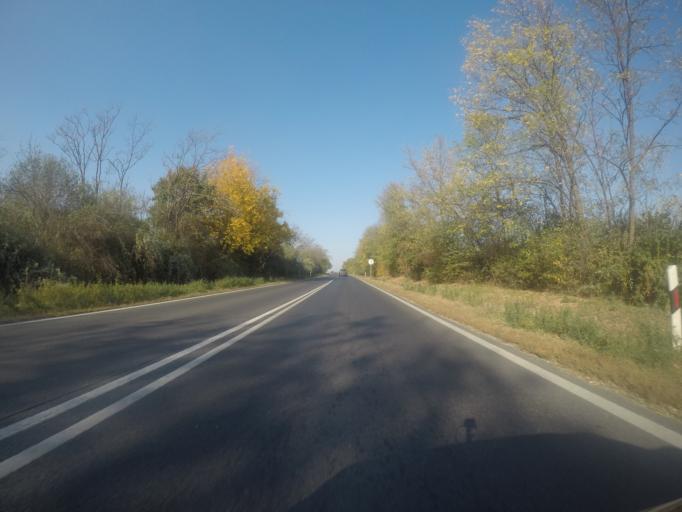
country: HU
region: Tolna
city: Dunafoldvar
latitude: 46.8367
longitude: 18.9097
